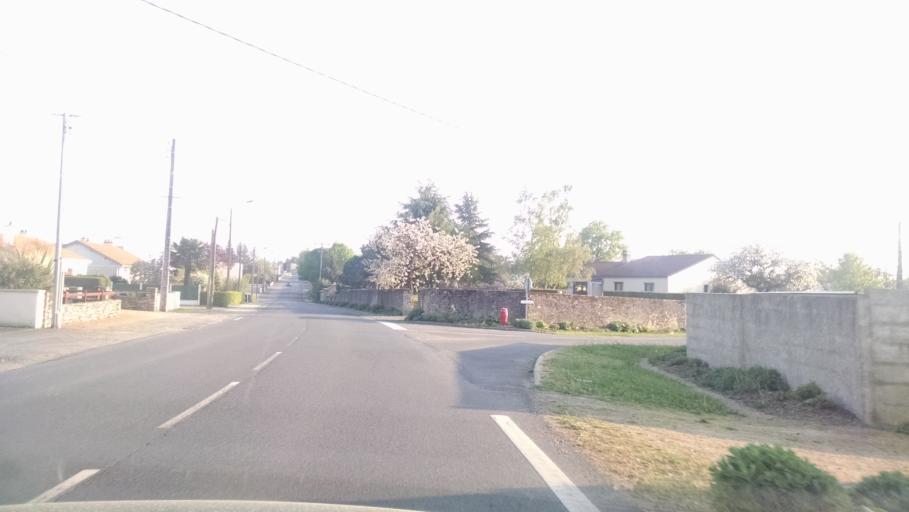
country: FR
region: Pays de la Loire
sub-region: Departement de la Loire-Atlantique
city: Boussay
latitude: 47.0543
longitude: -1.1840
